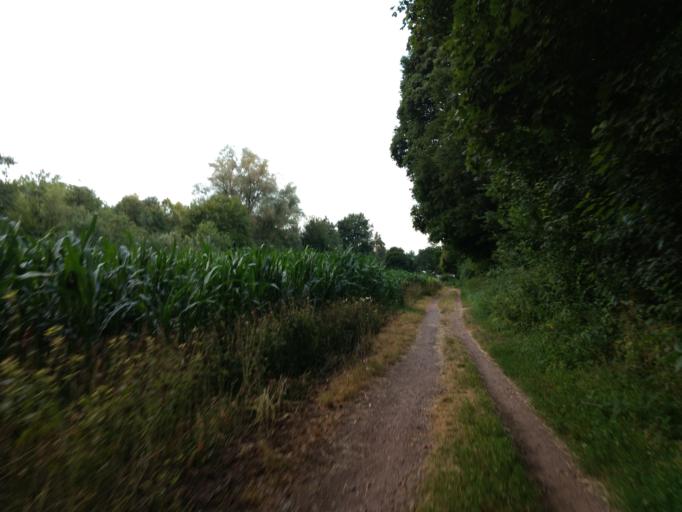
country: DE
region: Saarland
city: Wallerfangen
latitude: 49.3294
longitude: 6.7273
